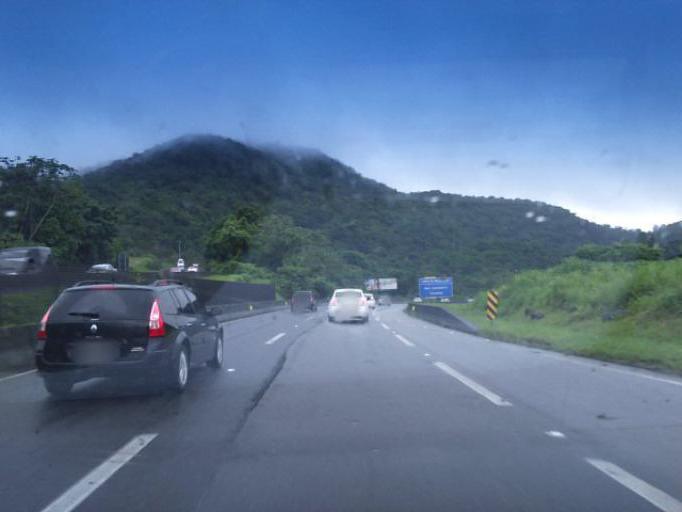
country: BR
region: Santa Catarina
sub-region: Itapema
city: Itapema
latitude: -27.0574
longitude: -48.5979
